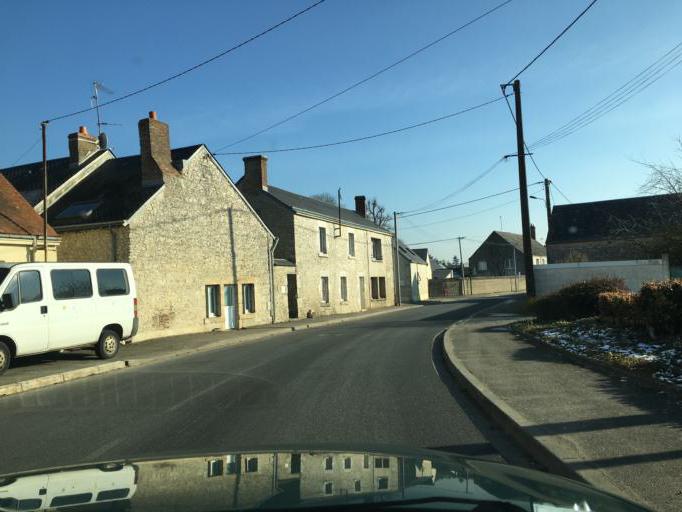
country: FR
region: Centre
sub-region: Departement du Loiret
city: Bricy
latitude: 48.0553
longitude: 1.7868
